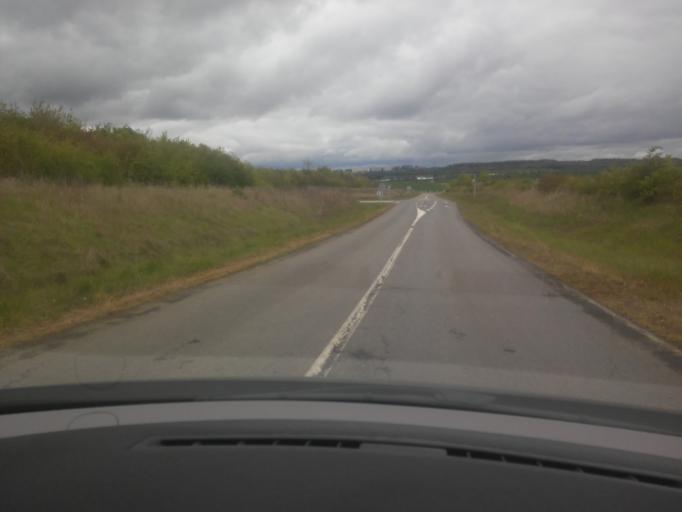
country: FR
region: Lorraine
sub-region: Departement de la Moselle
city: Mecleuves
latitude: 49.0498
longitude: 6.2570
